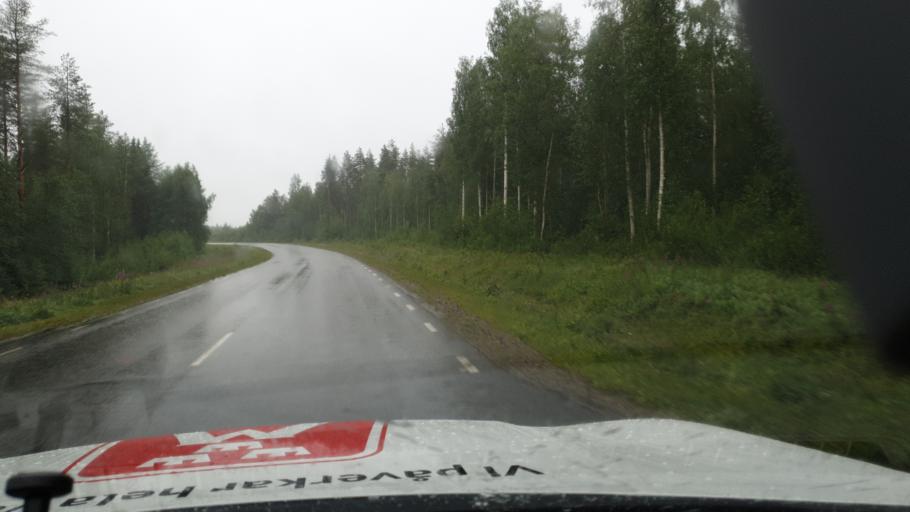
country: SE
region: Vaesterbotten
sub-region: Skelleftea Kommun
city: Langsele
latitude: 64.8246
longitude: 19.9304
